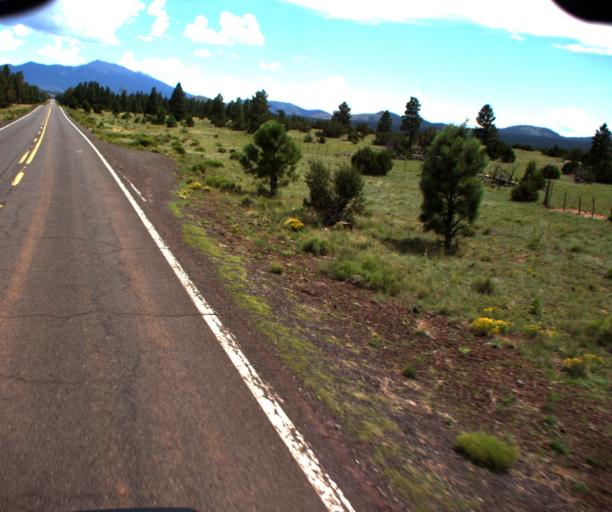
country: US
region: Arizona
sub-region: Coconino County
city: Parks
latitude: 35.4884
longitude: -111.8082
